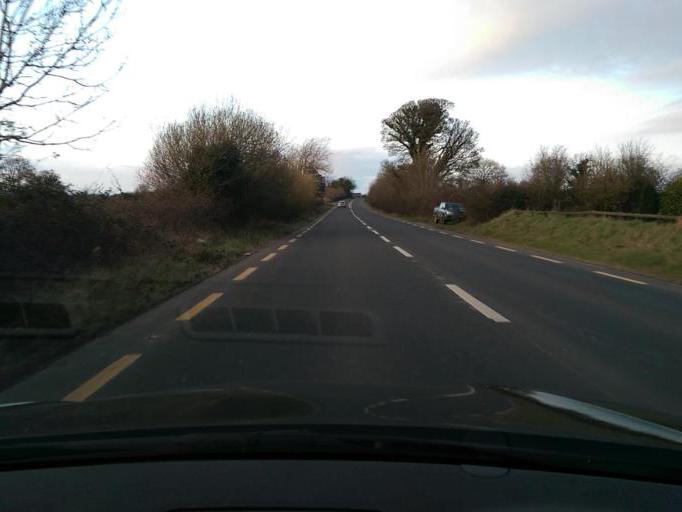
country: IE
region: Munster
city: Nenagh Bridge
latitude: 52.8959
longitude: -8.1878
